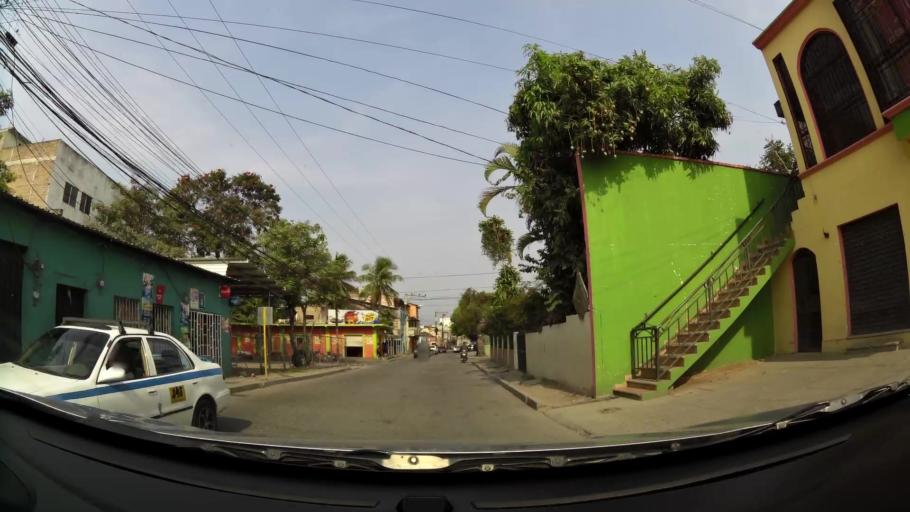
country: HN
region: Comayagua
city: Comayagua
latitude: 14.4562
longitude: -87.6386
